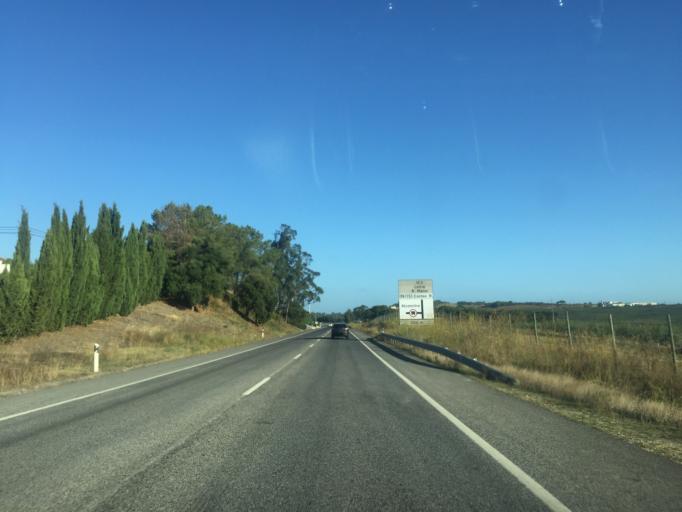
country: PT
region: Lisbon
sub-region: Azambuja
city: Alcoentre
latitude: 39.1989
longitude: -8.9530
